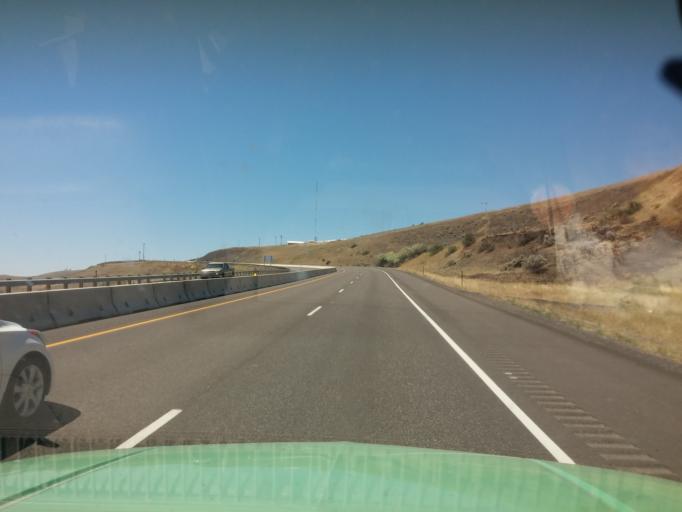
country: US
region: Idaho
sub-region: Nez Perce County
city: Lewiston
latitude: 46.4622
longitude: -116.9941
